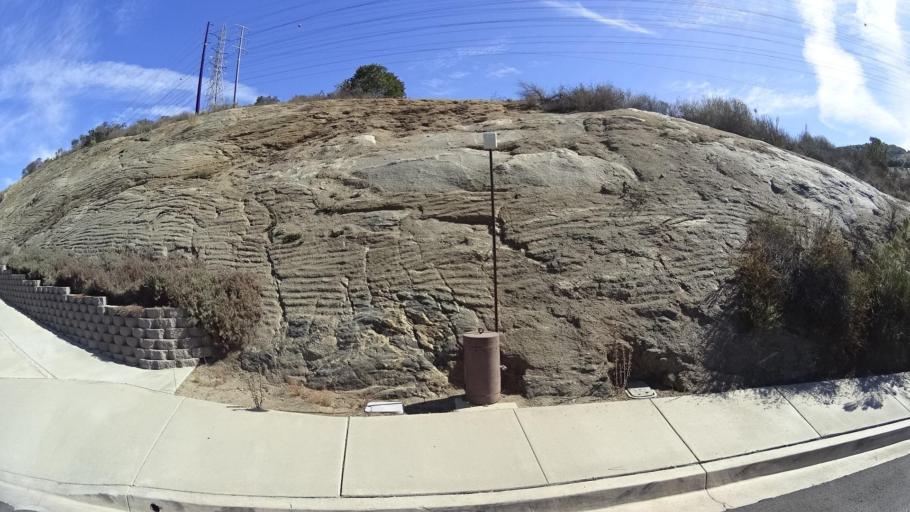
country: US
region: California
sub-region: San Diego County
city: Crest
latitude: 32.8330
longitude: -116.8874
